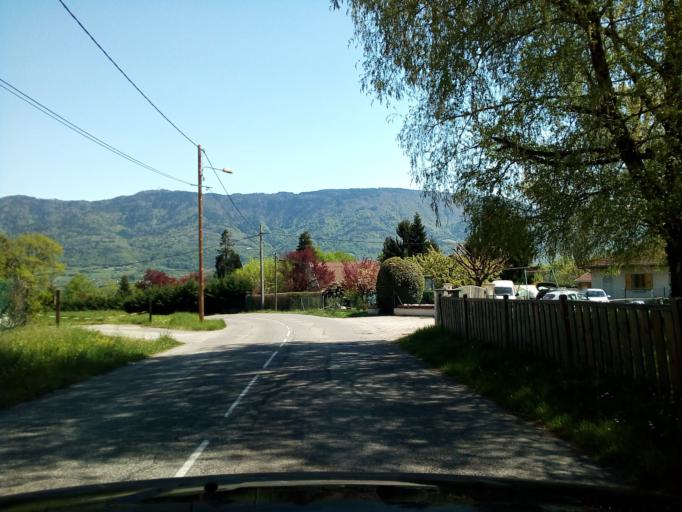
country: FR
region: Rhone-Alpes
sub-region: Departement de l'Isere
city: Barraux
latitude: 45.4292
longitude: 5.9851
